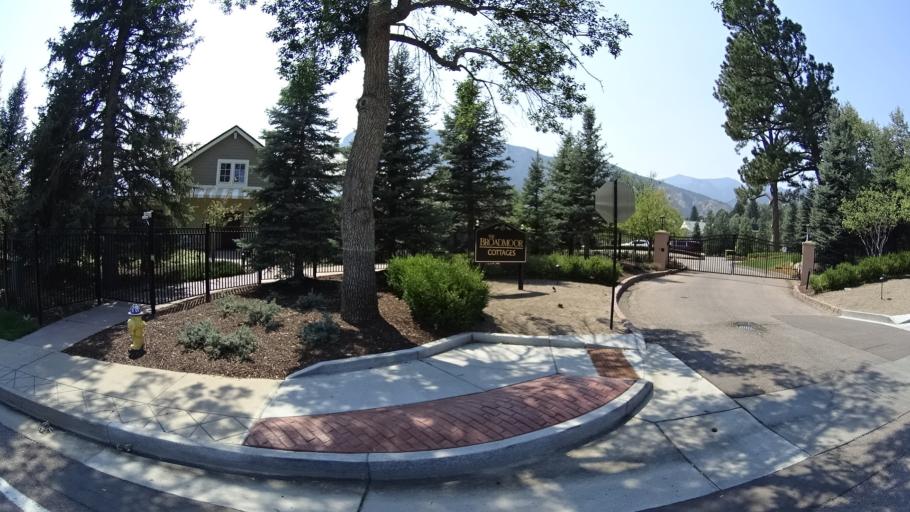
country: US
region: Colorado
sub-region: El Paso County
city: Colorado Springs
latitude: 38.7891
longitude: -104.8475
